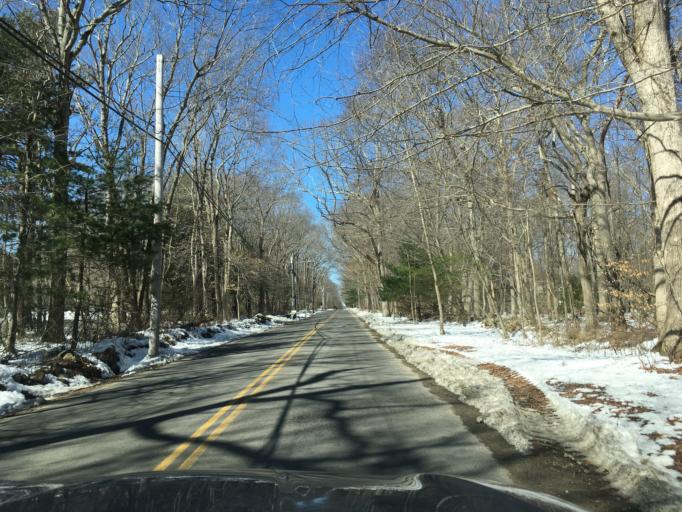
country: US
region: Rhode Island
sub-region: Washington County
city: Exeter
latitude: 41.6071
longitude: -71.5345
